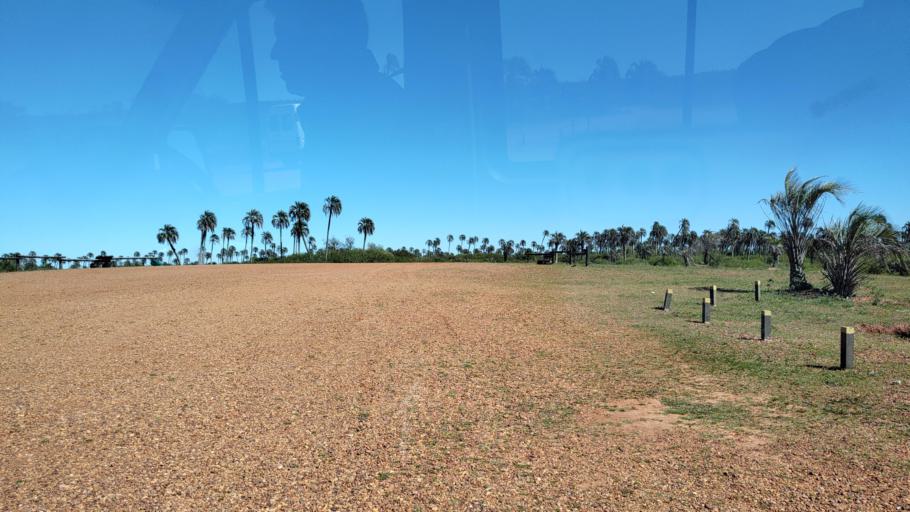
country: AR
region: Entre Rios
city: Ubajay
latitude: -31.8911
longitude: -58.2412
